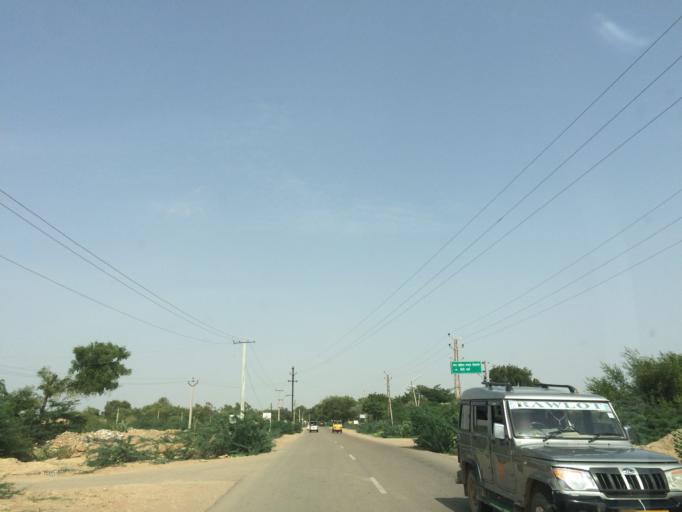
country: IN
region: Rajasthan
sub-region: Jaisalmer
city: Jaisalmer
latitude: 26.9113
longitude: 70.9277
